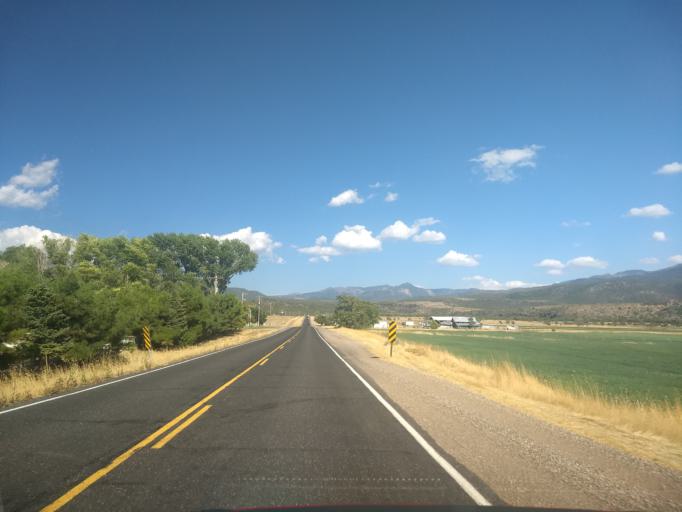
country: US
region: Utah
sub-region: Washington County
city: Enterprise
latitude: 37.4170
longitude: -113.6215
